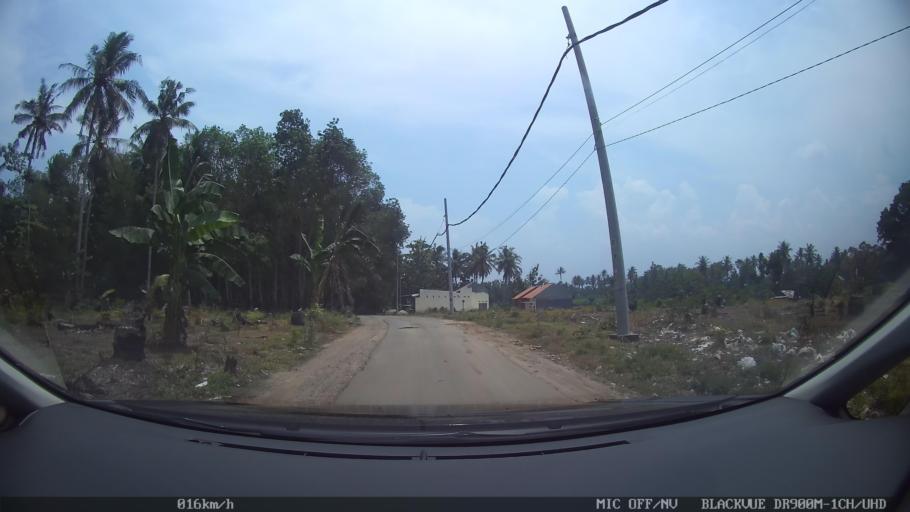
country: ID
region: Lampung
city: Natar
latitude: -5.3154
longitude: 105.2463
